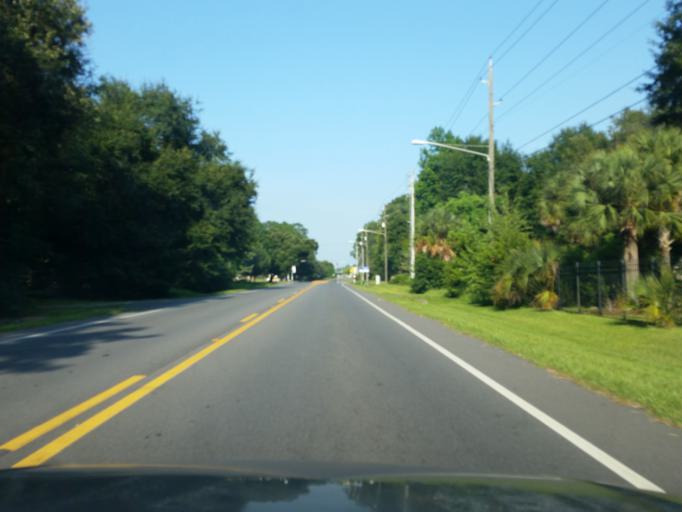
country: US
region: Alabama
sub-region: Baldwin County
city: Foley
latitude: 30.4066
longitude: -87.6942
